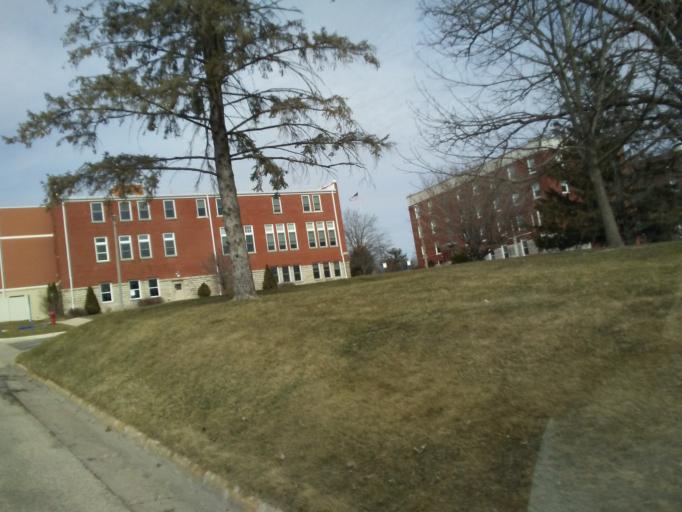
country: US
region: Iowa
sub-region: Winneshiek County
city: Decorah
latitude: 43.3098
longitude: -91.8065
